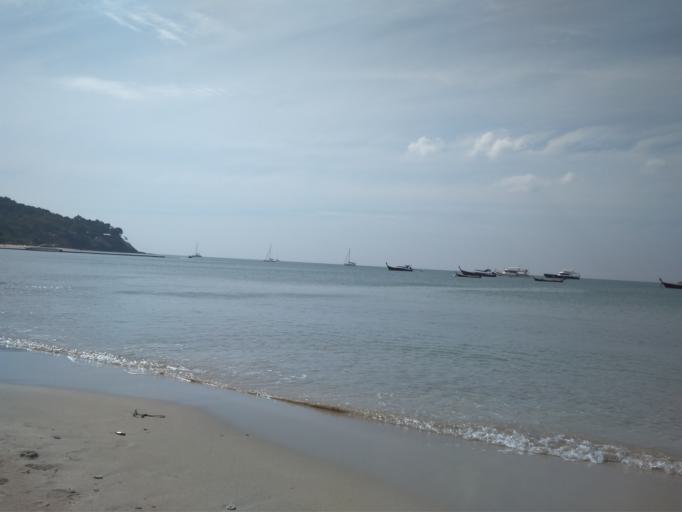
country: TH
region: Krabi
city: Ko Lanta
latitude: 7.4979
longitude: 99.0725
